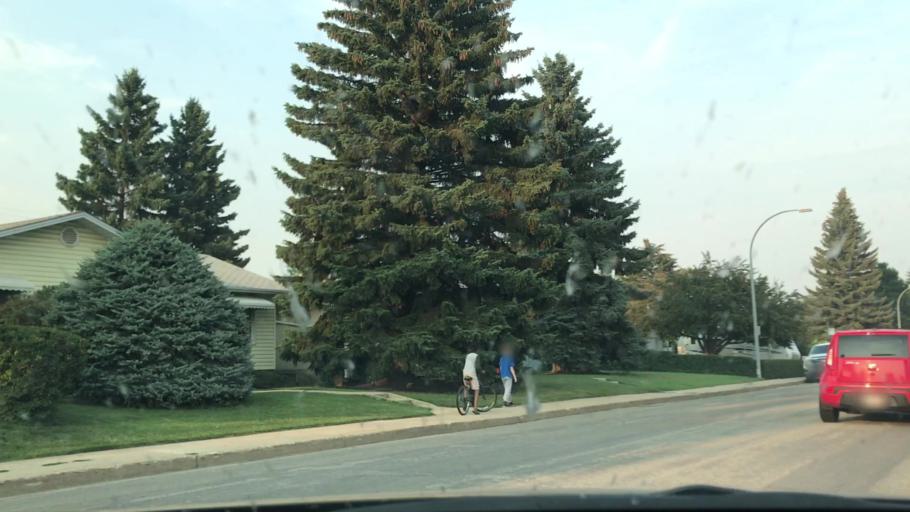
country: CA
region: Alberta
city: Edmonton
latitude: 53.5212
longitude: -113.4382
